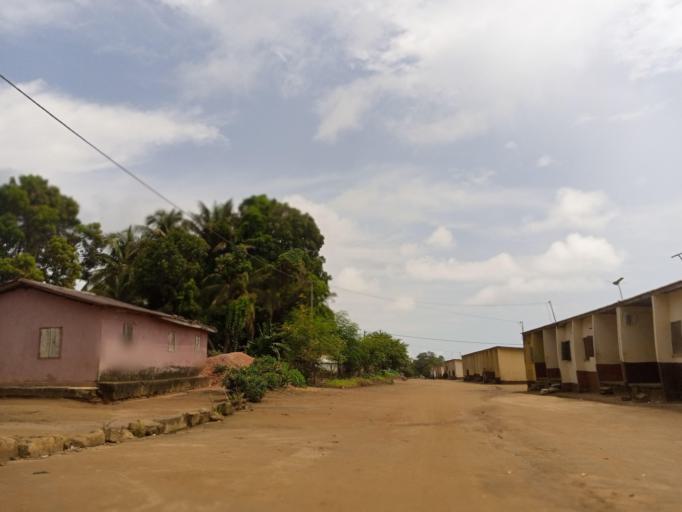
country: SL
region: Northern Province
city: Sawkta
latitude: 8.6292
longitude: -13.2051
